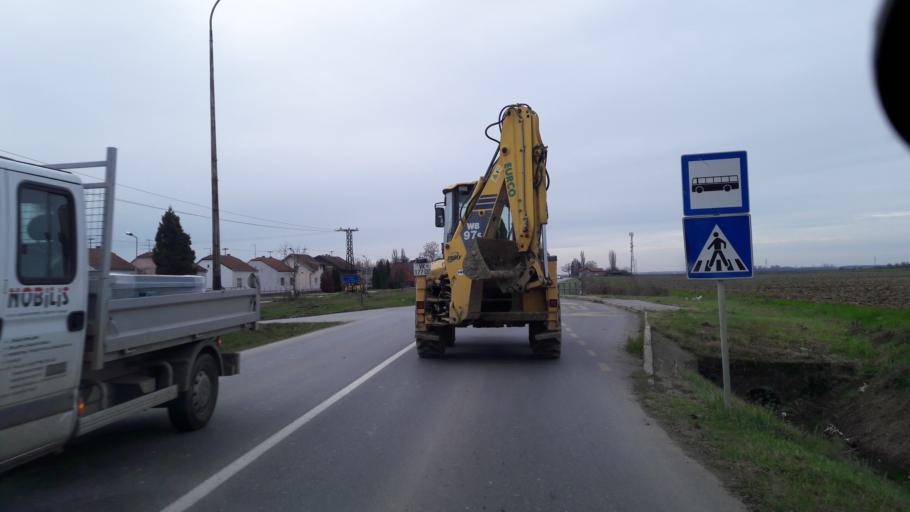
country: HR
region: Osjecko-Baranjska
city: Ovcara
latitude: 45.5085
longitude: 18.5663
